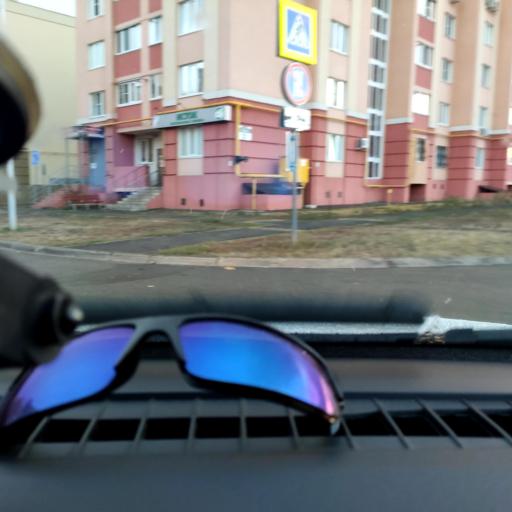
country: RU
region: Samara
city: Samara
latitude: 53.1188
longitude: 50.1565
